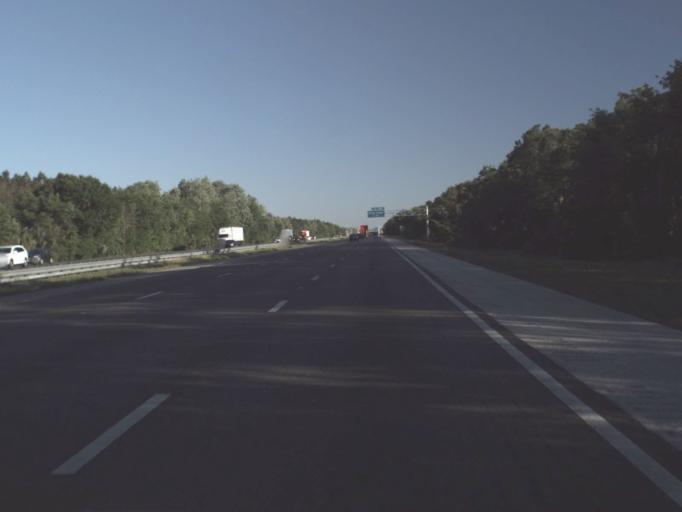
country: US
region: Florida
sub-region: Flagler County
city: Palm Coast
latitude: 29.6179
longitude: -81.2582
